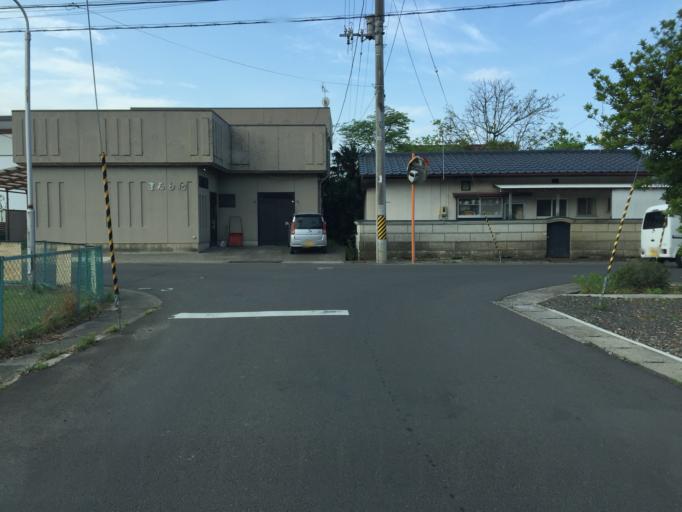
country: JP
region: Fukushima
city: Yanagawamachi-saiwaicho
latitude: 37.8540
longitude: 140.6037
